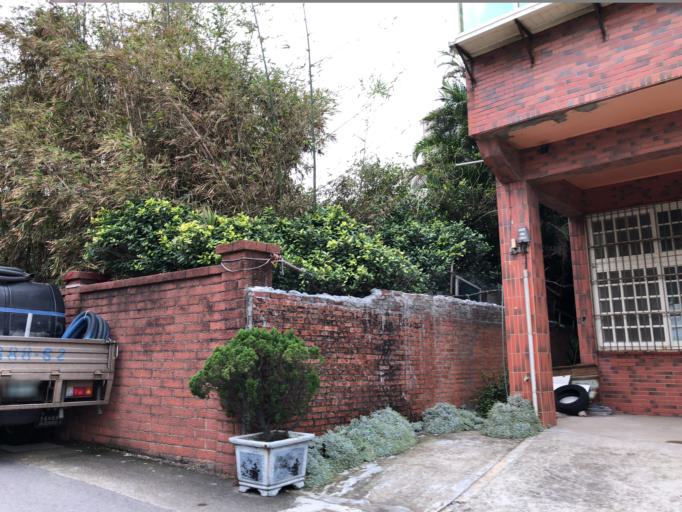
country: TW
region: Taiwan
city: Taoyuan City
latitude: 25.1099
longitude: 121.2417
